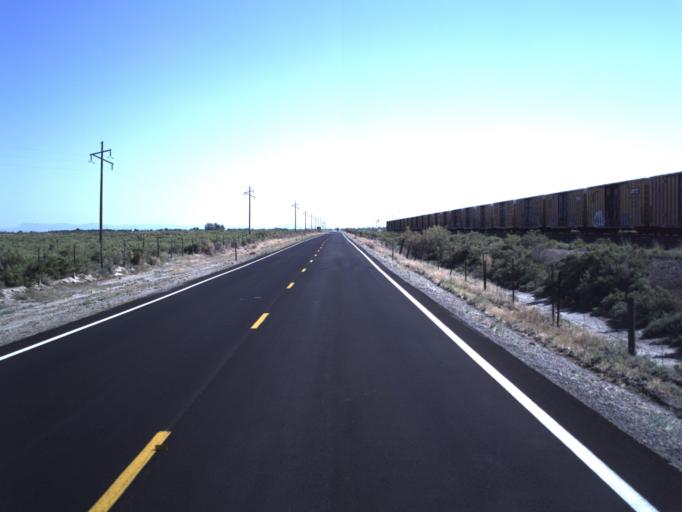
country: US
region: Utah
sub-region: Millard County
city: Delta
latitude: 39.2377
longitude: -112.6645
